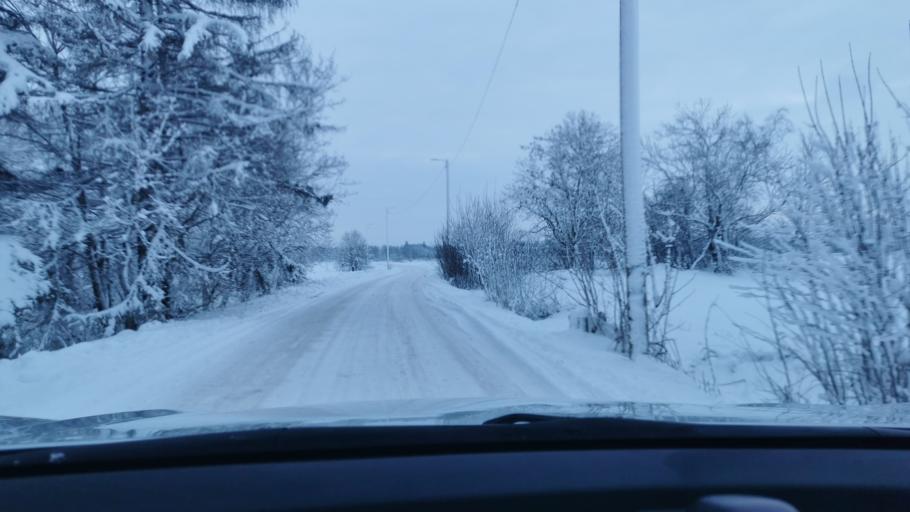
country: EE
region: Laeaene-Virumaa
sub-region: Someru vald
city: Someru
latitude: 59.4524
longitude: 26.4151
